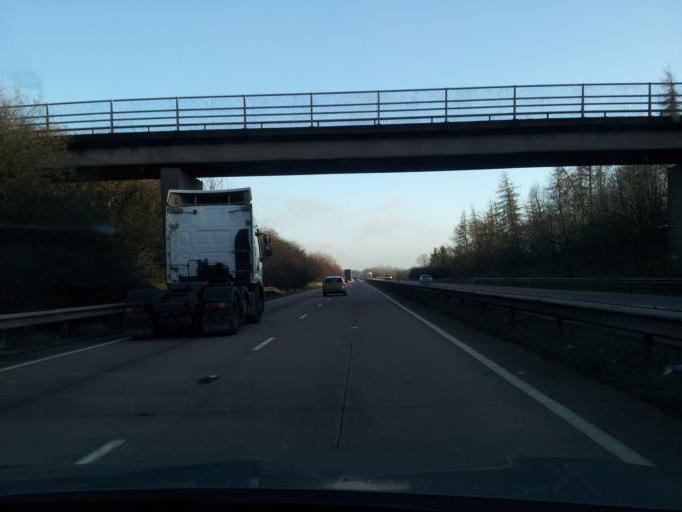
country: GB
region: England
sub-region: Staffordshire
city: Cheadle
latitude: 52.9392
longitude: -1.9905
